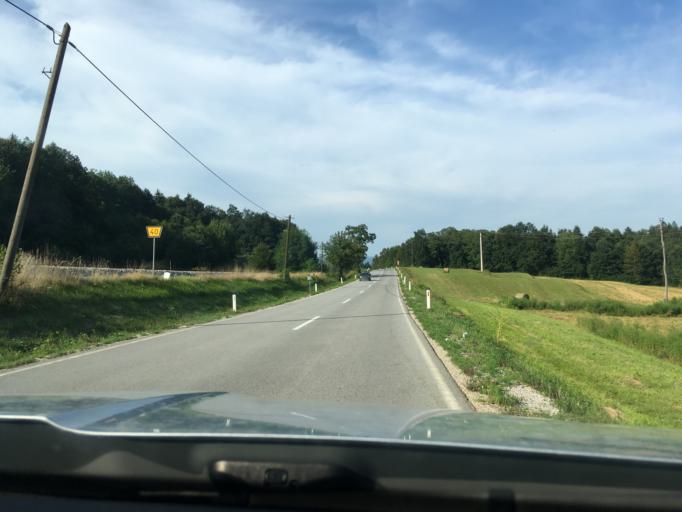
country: SI
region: Crnomelj
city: Crnomelj
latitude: 45.6052
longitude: 15.2389
